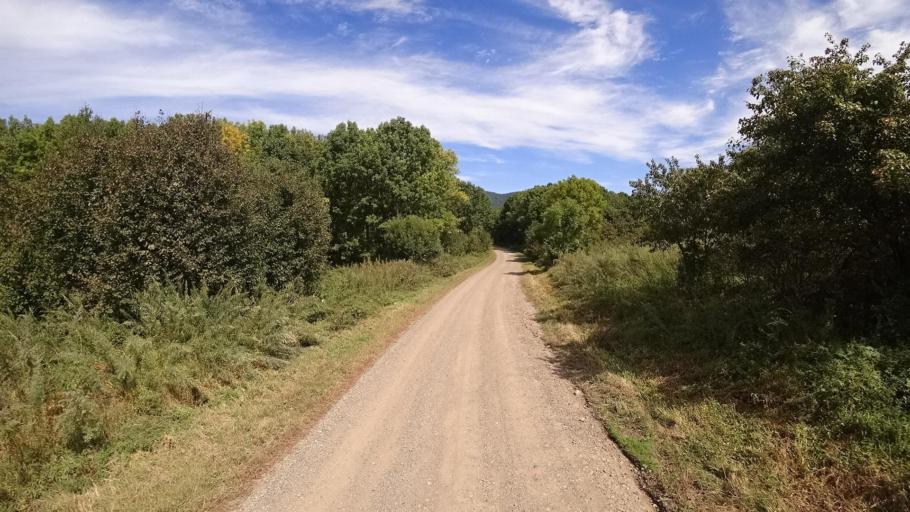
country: RU
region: Primorskiy
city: Yakovlevka
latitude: 44.6586
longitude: 133.7467
